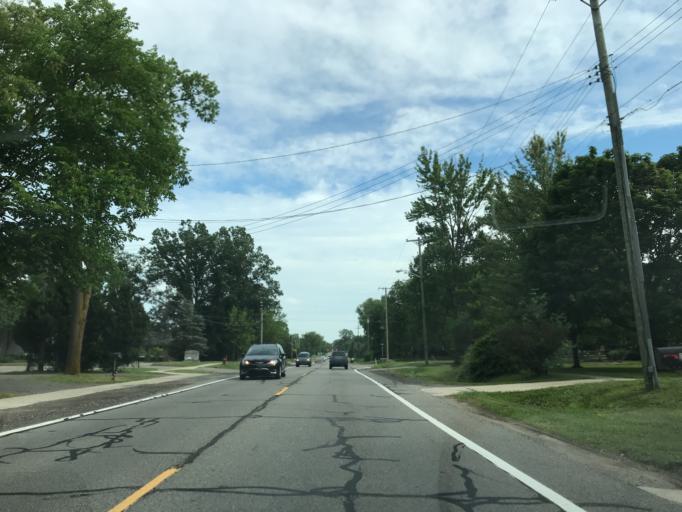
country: US
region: Michigan
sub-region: Oakland County
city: Farmington
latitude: 42.4654
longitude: -83.3375
